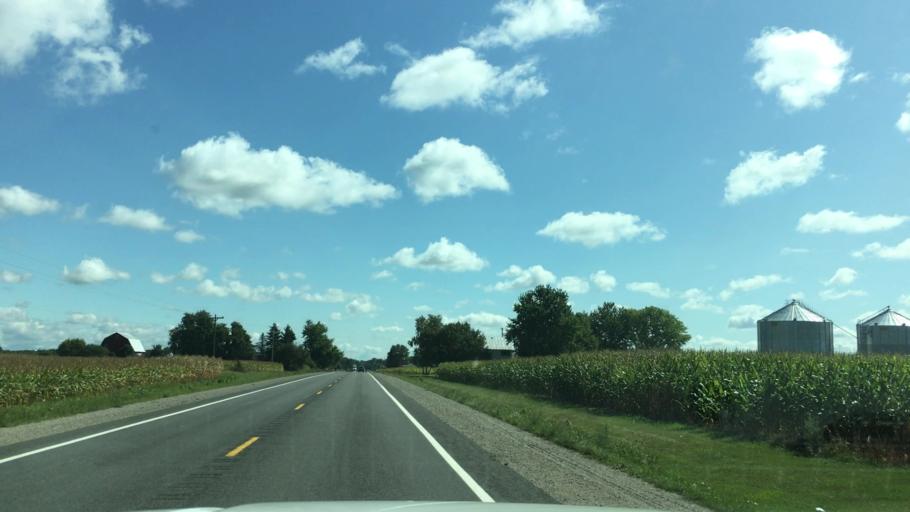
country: US
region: Michigan
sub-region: Montcalm County
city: Carson City
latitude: 43.1772
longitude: -84.8855
